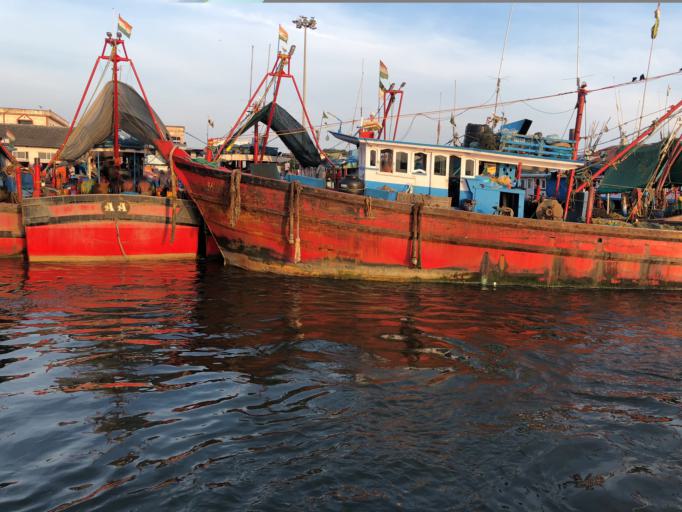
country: IN
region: Karnataka
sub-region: Dakshina Kannada
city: Ullal
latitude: 12.8541
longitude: 74.8328
